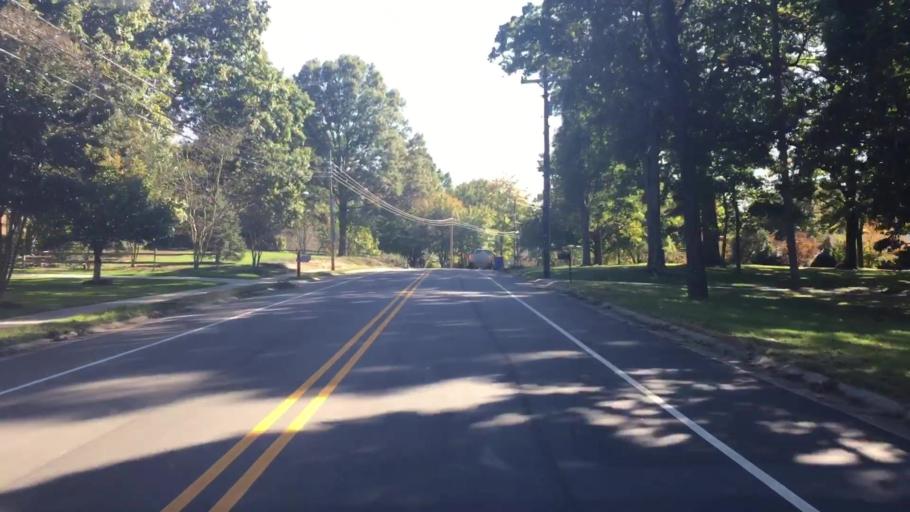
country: US
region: North Carolina
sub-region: Iredell County
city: Mooresville
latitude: 35.5699
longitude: -80.8015
